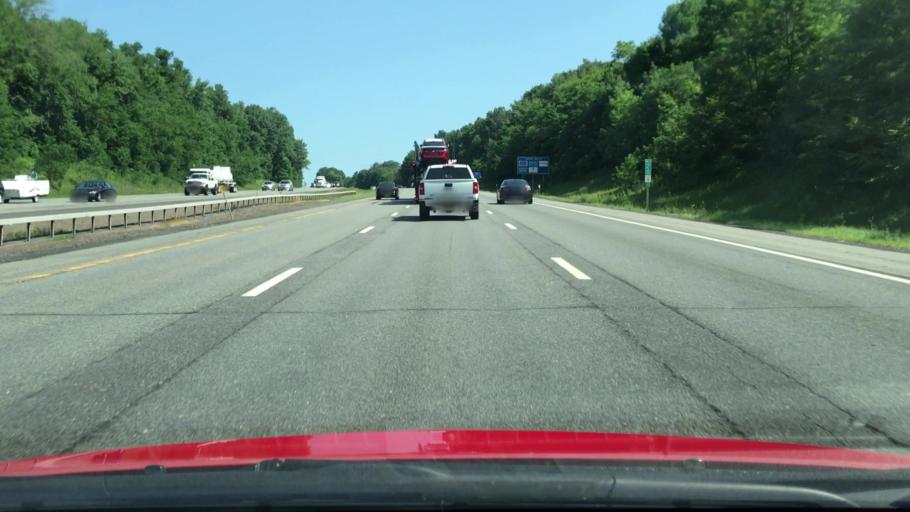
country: US
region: New York
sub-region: Saratoga County
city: Country Knolls
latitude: 42.9574
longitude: -73.8017
